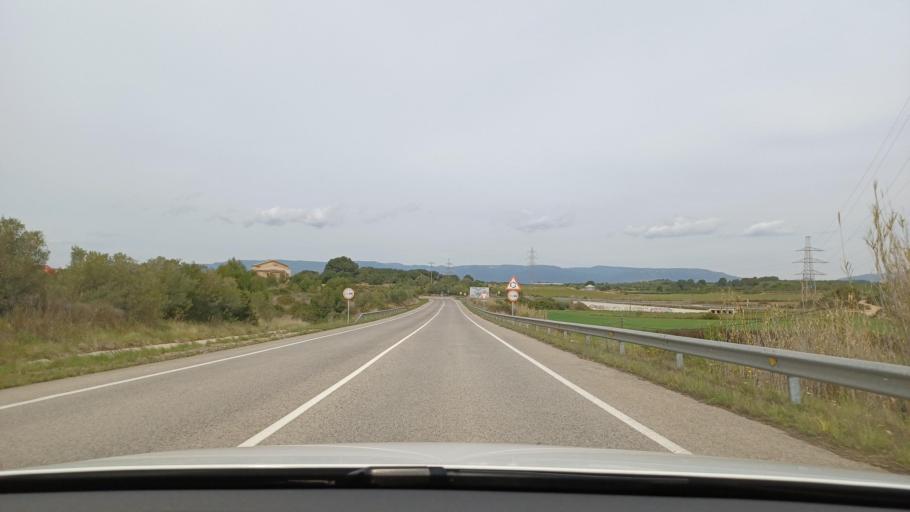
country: ES
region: Catalonia
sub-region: Provincia de Tarragona
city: La Secuita
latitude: 41.1943
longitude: 1.2652
